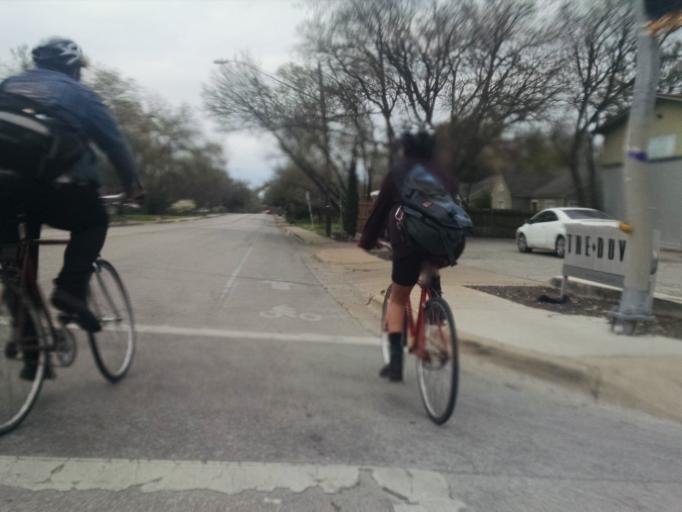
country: US
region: Texas
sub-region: Travis County
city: Austin
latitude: 30.3143
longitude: -97.7200
